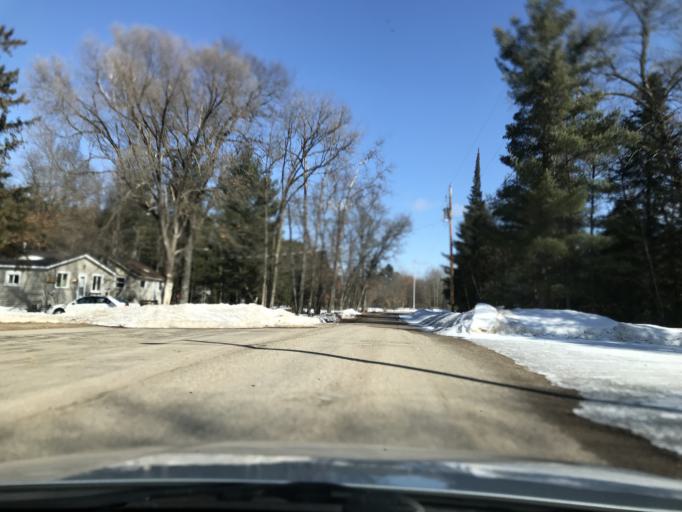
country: US
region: Wisconsin
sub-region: Marinette County
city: Niagara
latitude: 45.4236
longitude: -88.0948
